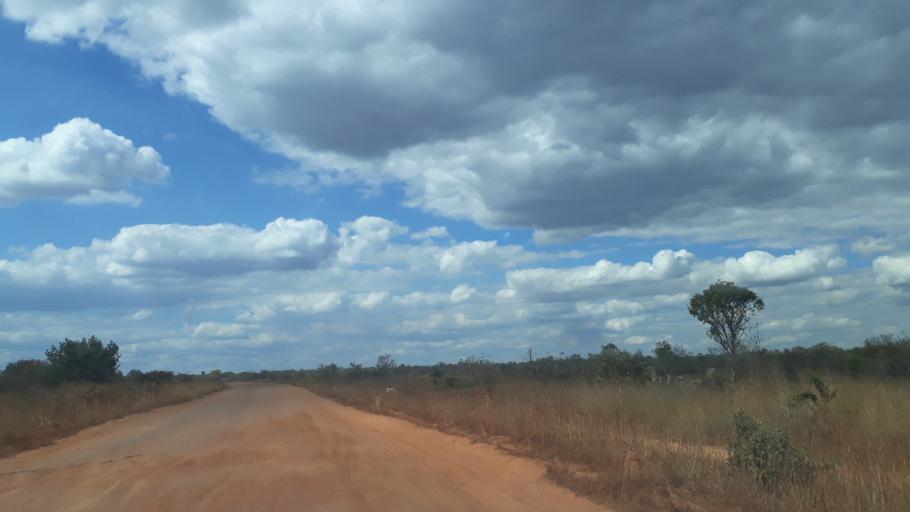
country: ZM
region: Copperbelt
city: Mufulira
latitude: -11.9957
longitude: 28.7256
